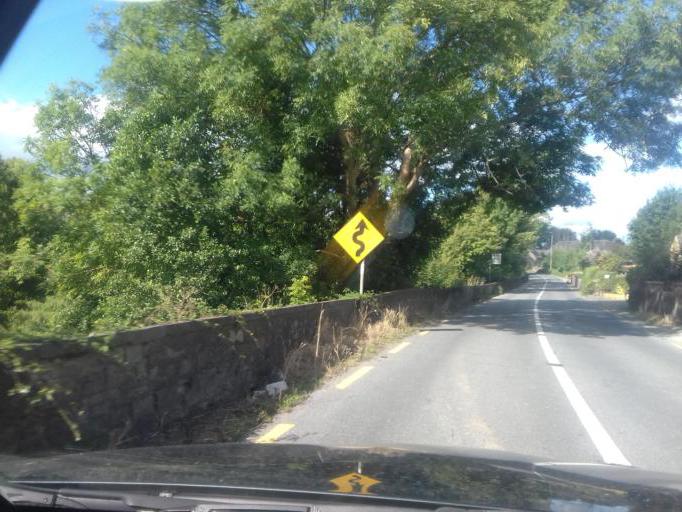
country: IE
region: Leinster
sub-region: Kilkenny
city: Thomastown
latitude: 52.5091
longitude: -7.1594
